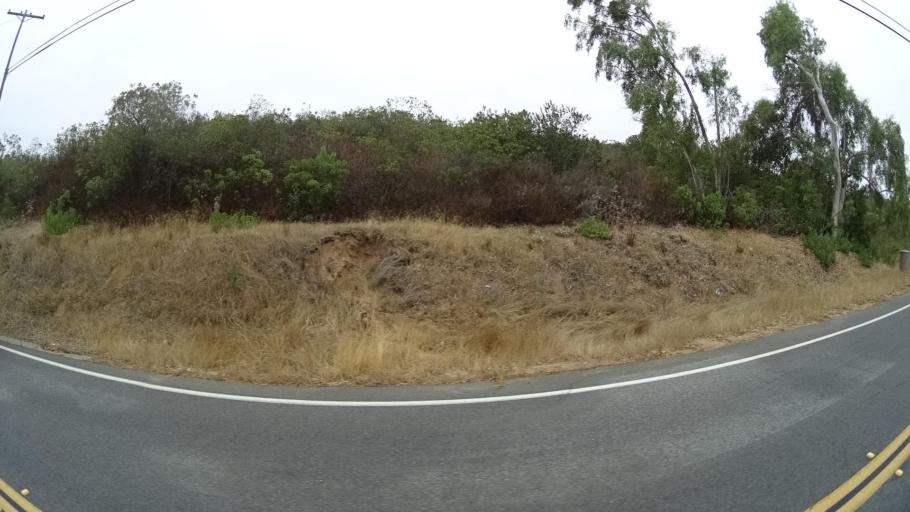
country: US
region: California
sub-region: San Diego County
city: Lake San Marcos
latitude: 33.0785
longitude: -117.1726
